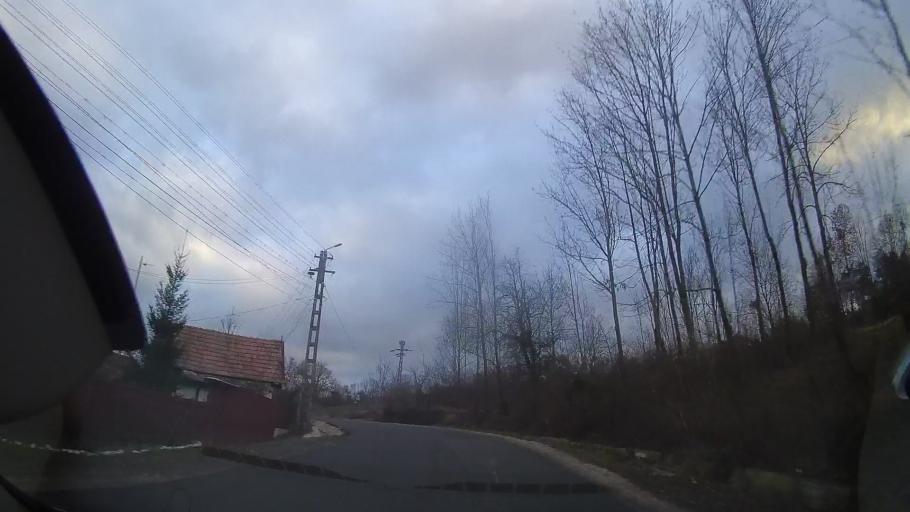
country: RO
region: Cluj
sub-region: Comuna Calatele
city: Calatele
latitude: 46.7823
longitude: 23.0224
